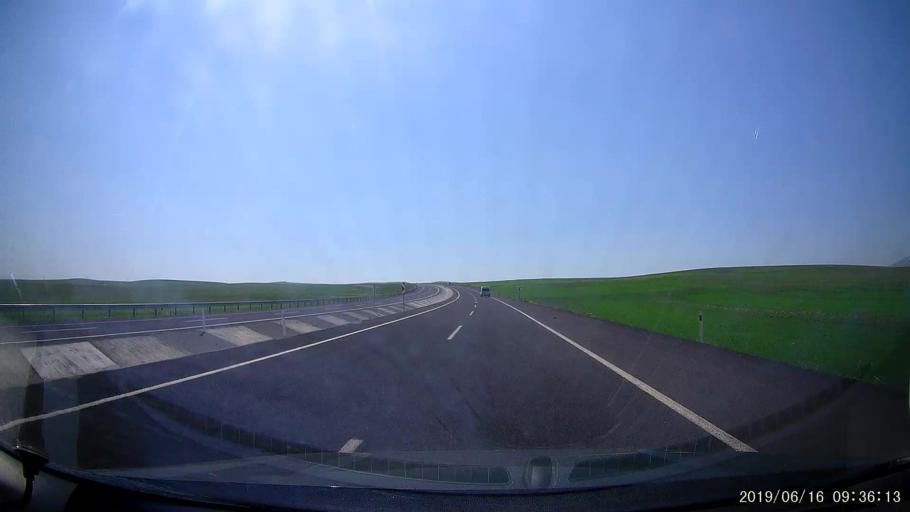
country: TR
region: Kars
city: Kars
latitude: 40.5602
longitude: 43.1685
